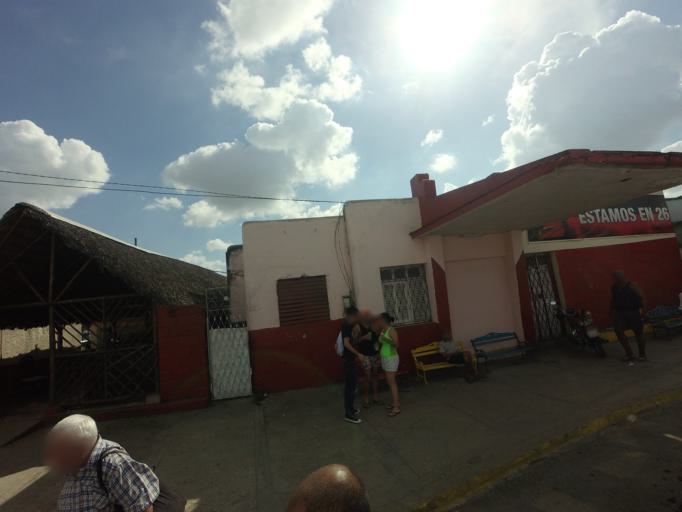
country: CU
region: Artemisa
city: Bauta
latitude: 22.9797
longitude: -82.5482
